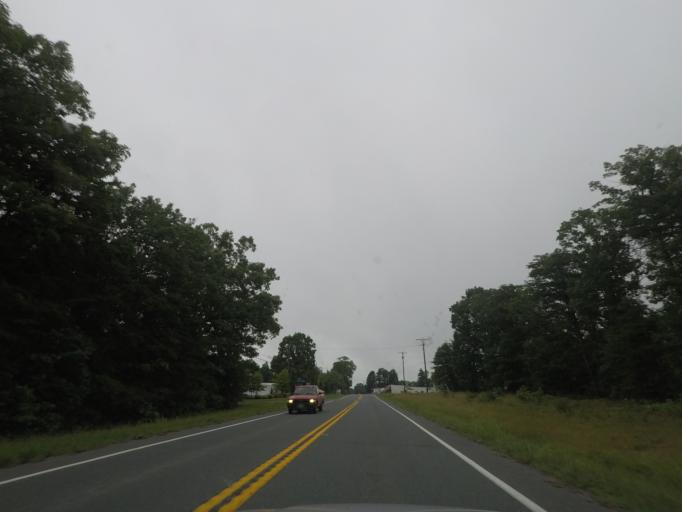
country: US
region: Virginia
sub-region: Fluvanna County
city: Weber City
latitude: 37.7460
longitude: -78.2883
